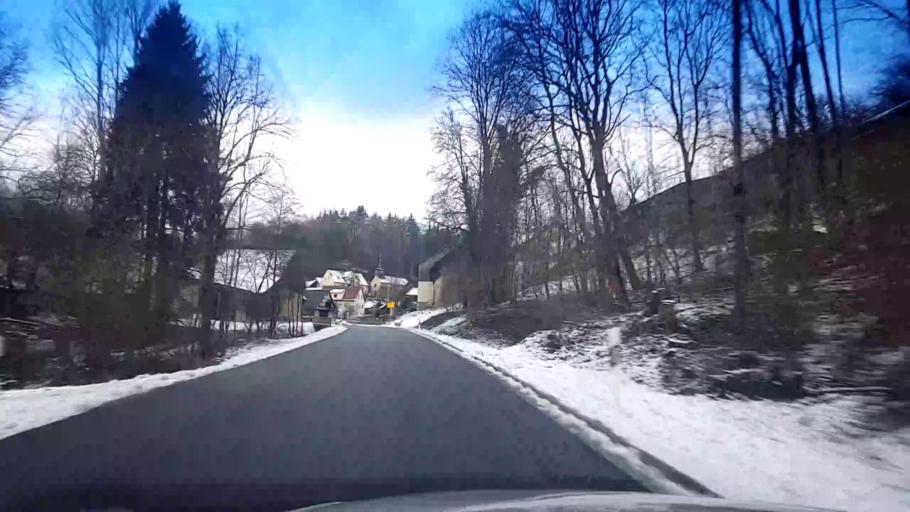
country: DE
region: Bavaria
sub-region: Upper Franconia
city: Buttenheim
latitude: 49.8489
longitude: 11.0790
